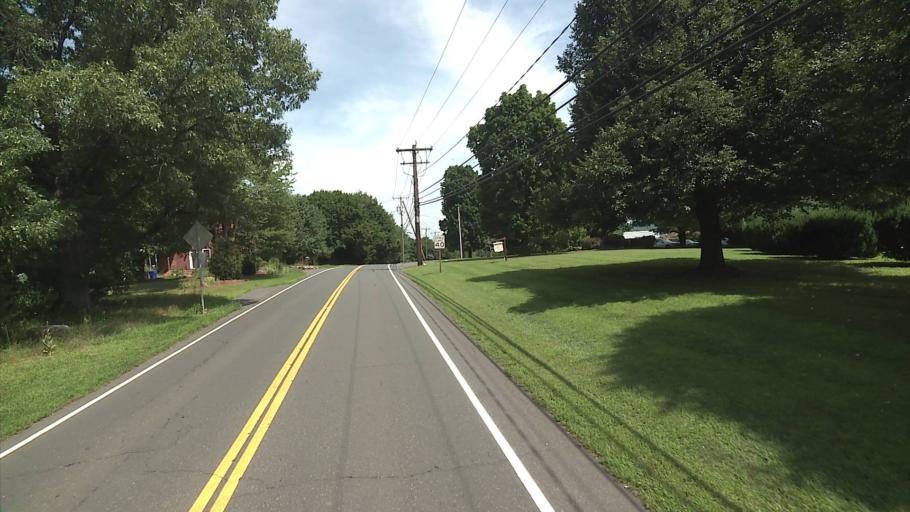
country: US
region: Connecticut
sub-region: Tolland County
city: Ellington
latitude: 41.8711
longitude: -72.4907
